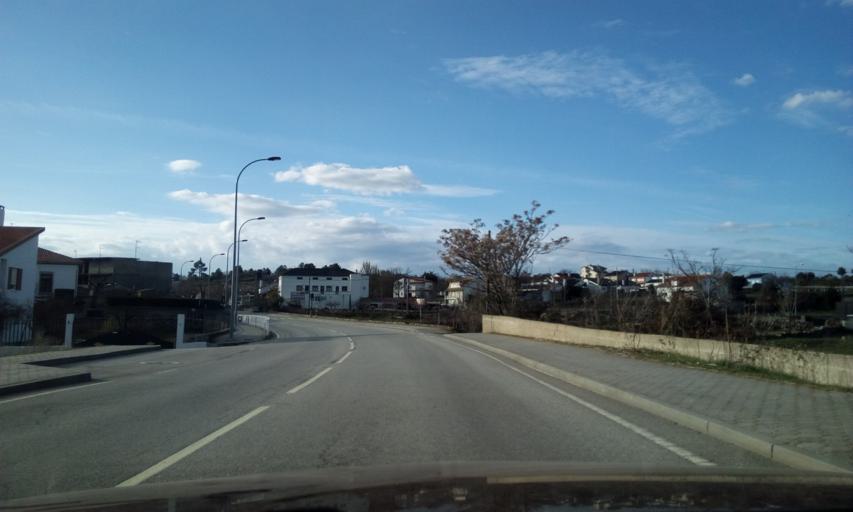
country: ES
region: Castille and Leon
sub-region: Provincia de Salamanca
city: Fuentes de Onoro
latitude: 40.6135
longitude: -6.8340
